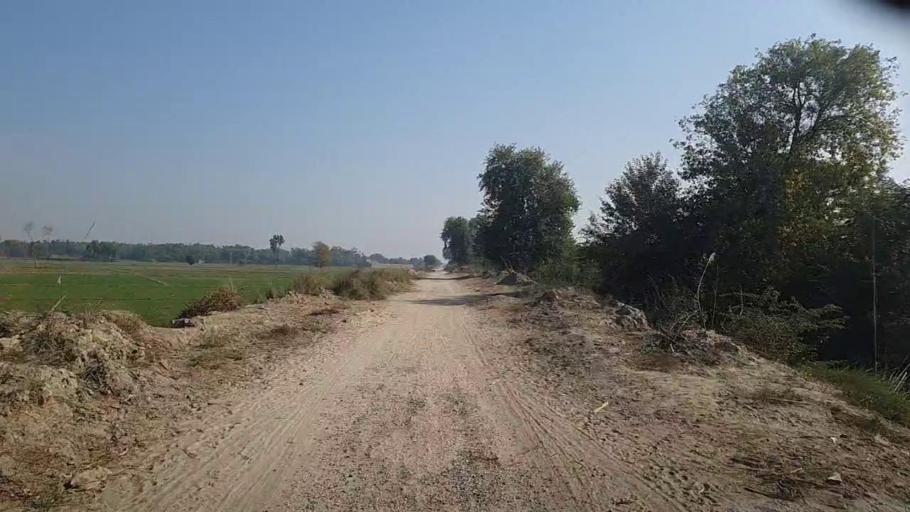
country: PK
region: Sindh
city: Darya Khan Marri
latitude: 26.7091
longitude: 68.3235
